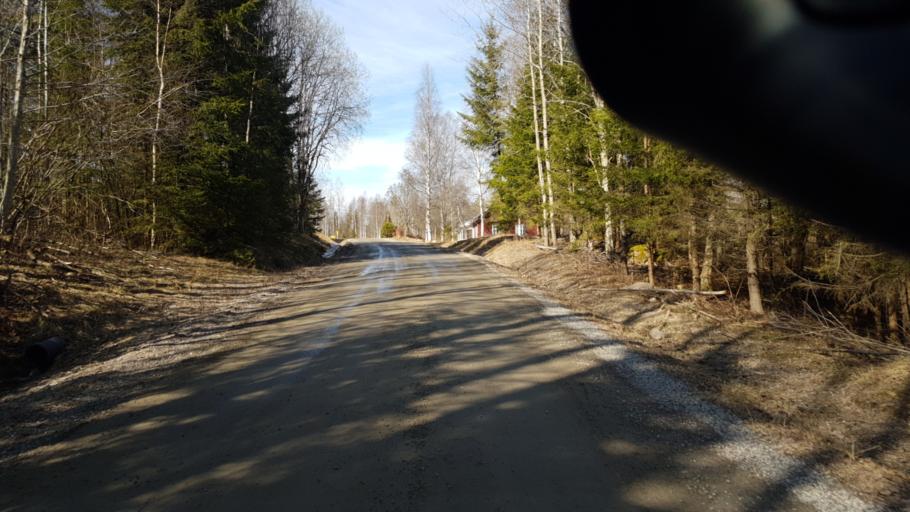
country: SE
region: Vaermland
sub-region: Sunne Kommun
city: Sunne
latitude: 59.6979
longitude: 12.8845
